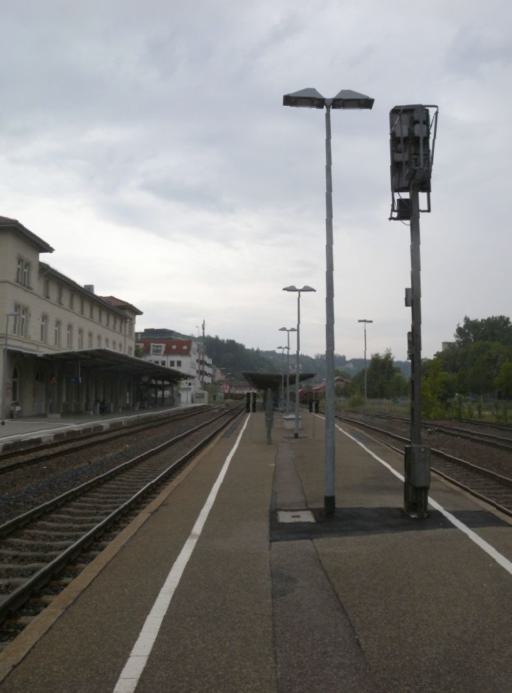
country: DE
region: Baden-Wuerttemberg
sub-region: Regierungsbezirk Stuttgart
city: Heidenheim an der Brenz
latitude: 48.6796
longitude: 10.1570
